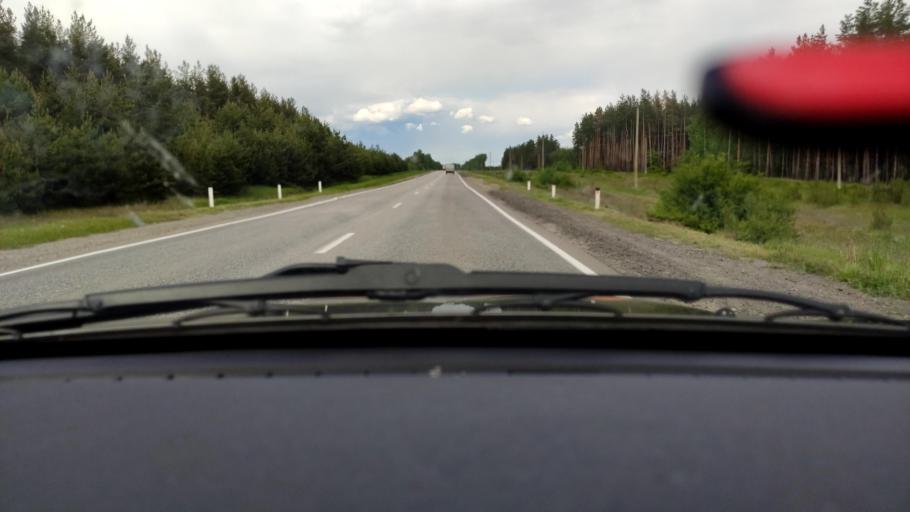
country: RU
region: Voronezj
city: Uryv-Pokrovka
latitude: 51.0549
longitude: 38.9879
